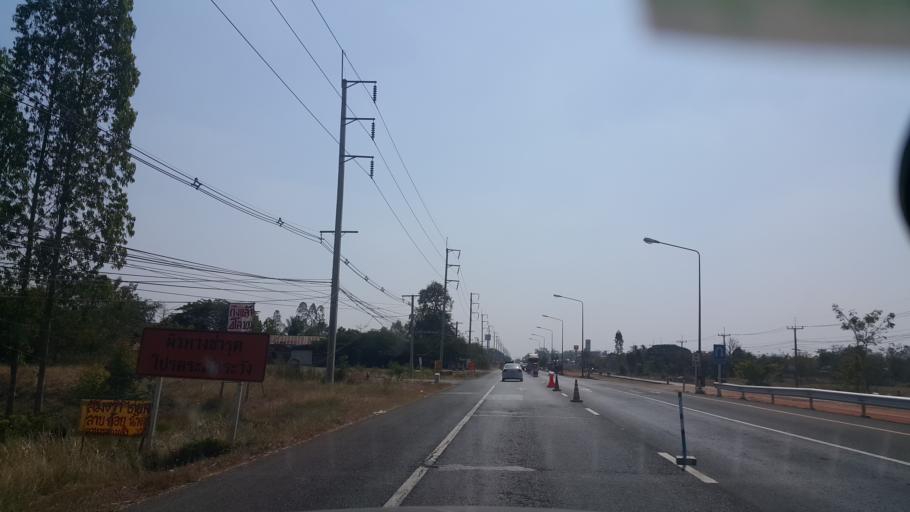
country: TH
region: Nakhon Ratchasima
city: Sida
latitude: 15.5746
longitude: 102.5548
